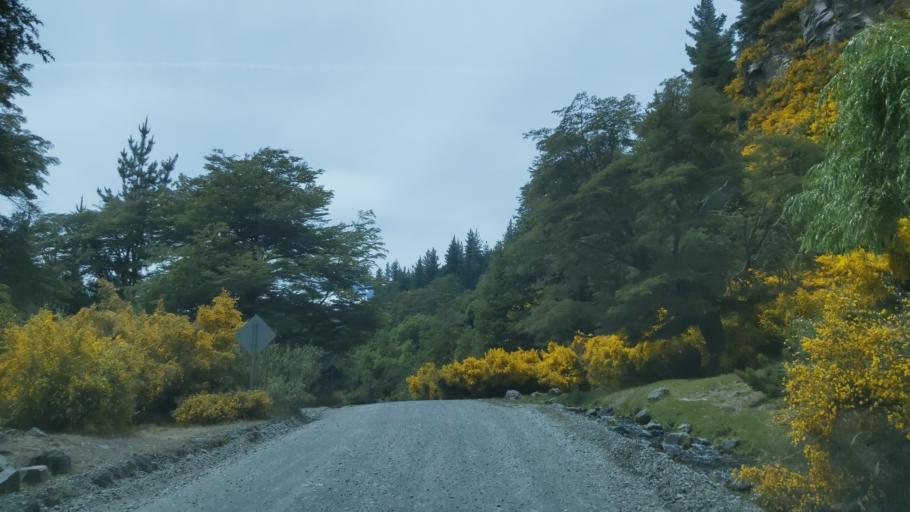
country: AR
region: Neuquen
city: Las Ovejas
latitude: -37.3966
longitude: -71.4544
